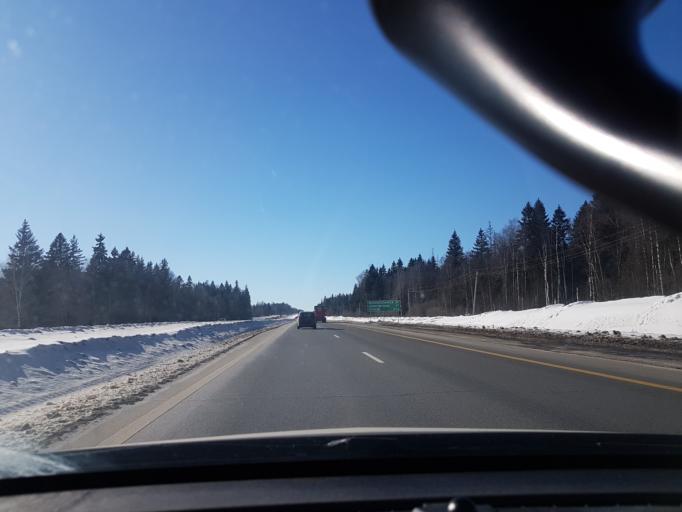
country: RU
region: Moskovskaya
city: Sychevo
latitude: 55.9853
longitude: 36.3291
